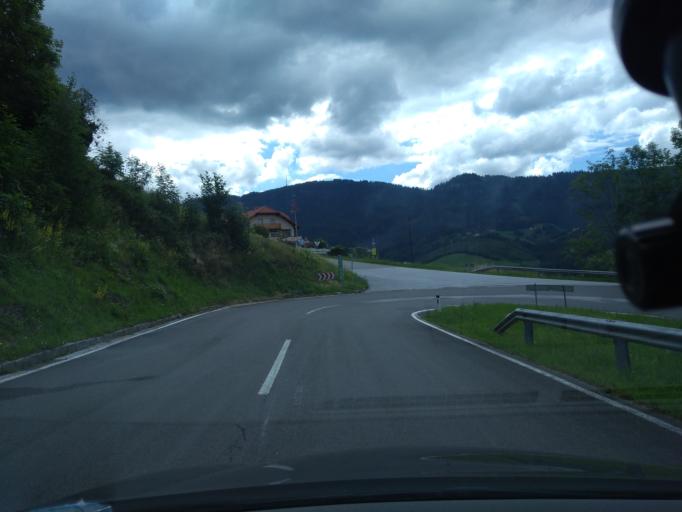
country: AT
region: Styria
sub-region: Politischer Bezirk Graz-Umgebung
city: Semriach
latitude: 47.2205
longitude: 15.4265
